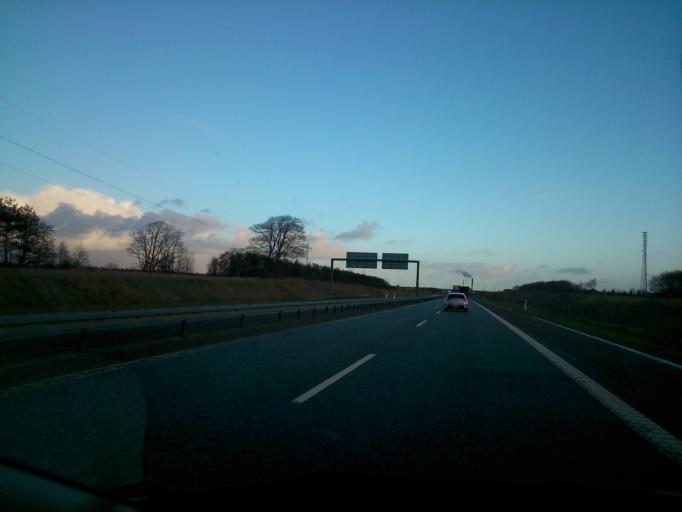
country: DK
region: Central Jutland
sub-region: Herning Kommune
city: Lind
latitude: 56.1142
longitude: 8.9654
